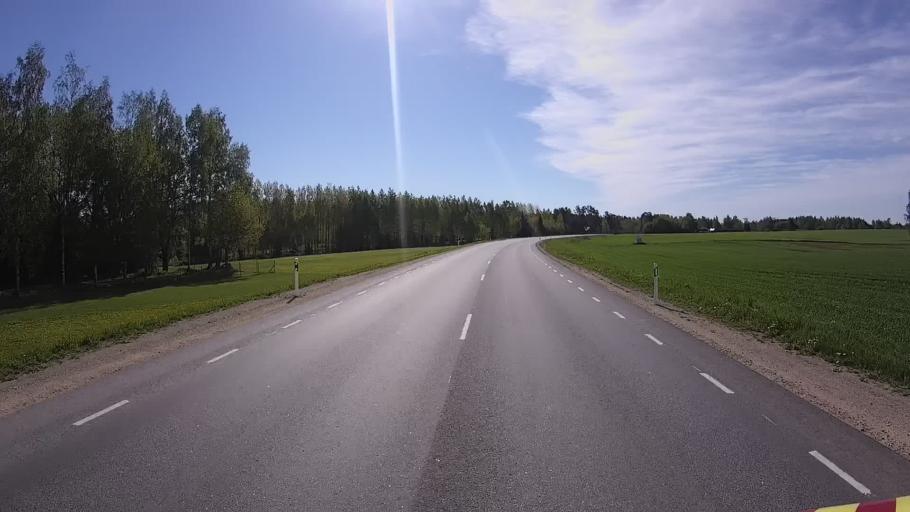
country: EE
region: Tartu
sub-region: UElenurme vald
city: Ulenurme
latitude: 58.3373
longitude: 26.9699
